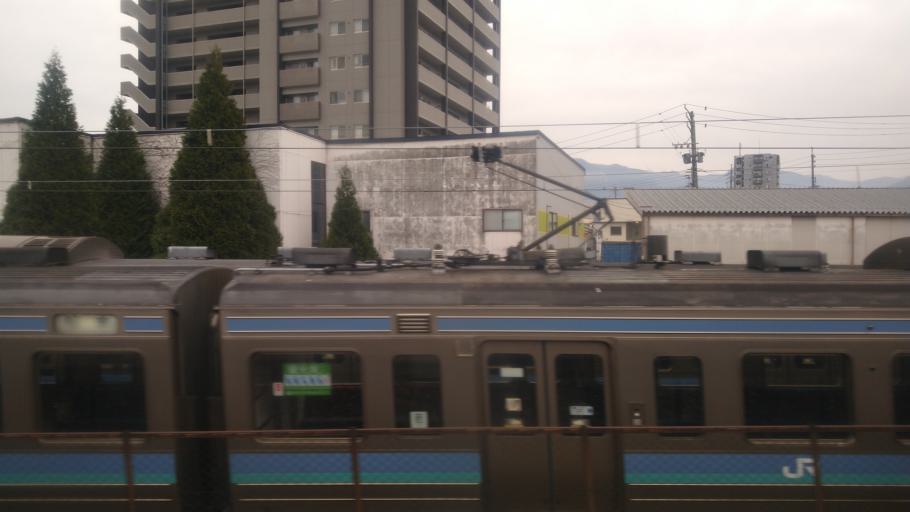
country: JP
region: Nagano
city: Matsumoto
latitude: 36.2258
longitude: 137.9672
